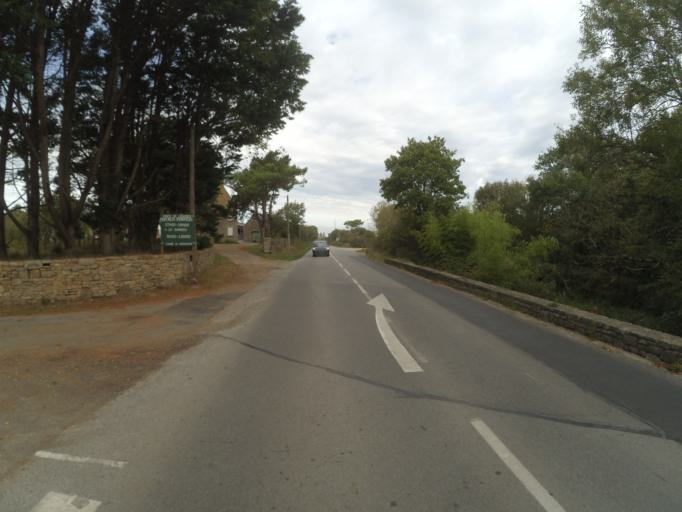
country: FR
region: Brittany
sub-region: Departement du Morbihan
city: Erdeven
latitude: 47.6519
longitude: -3.1653
